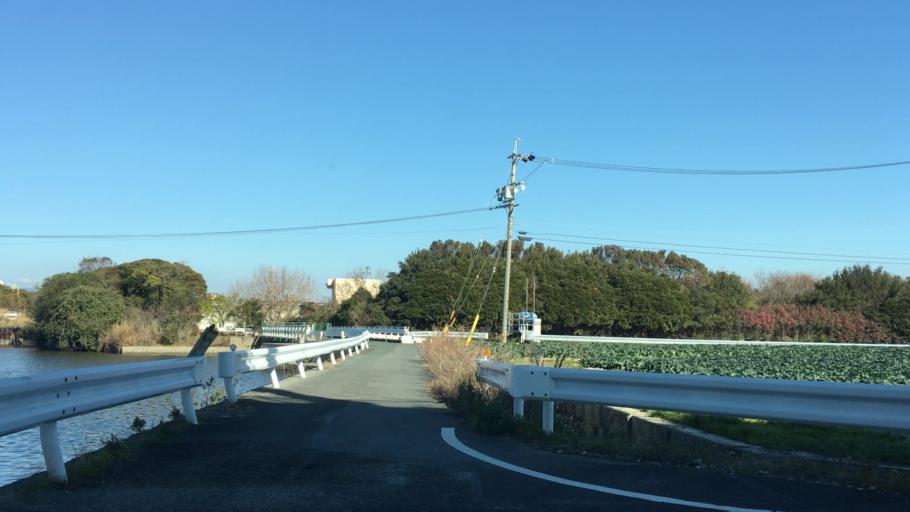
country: JP
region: Aichi
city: Toyohashi
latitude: 34.7327
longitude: 137.3512
